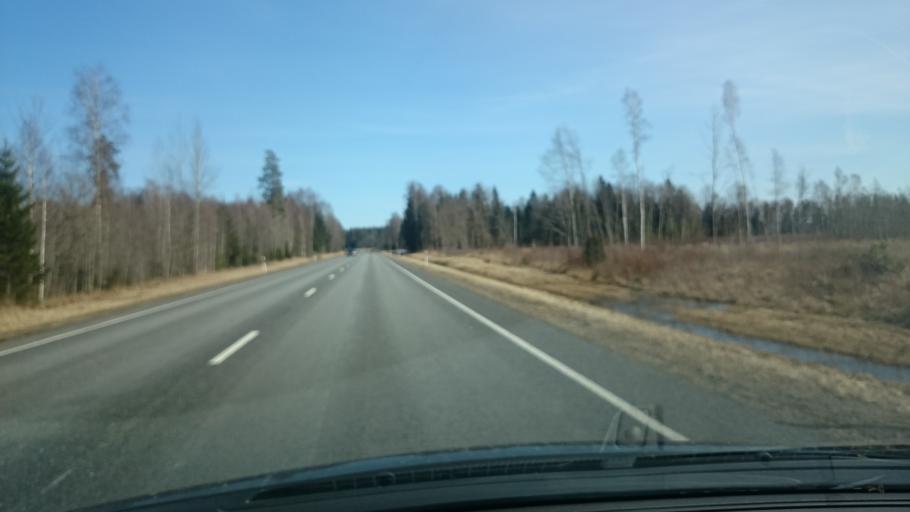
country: EE
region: Paernumaa
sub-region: Vaendra vald (alev)
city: Vandra
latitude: 58.6687
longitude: 25.0680
